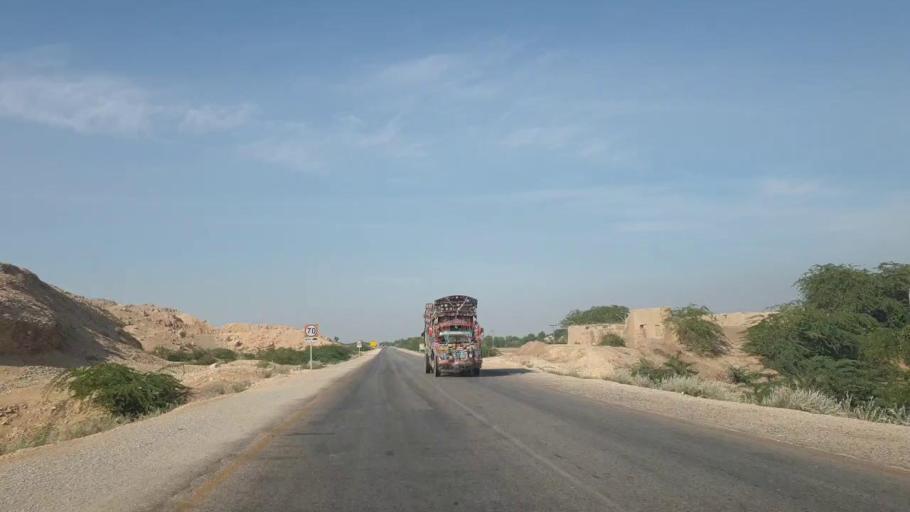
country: PK
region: Sindh
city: Sehwan
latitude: 26.3060
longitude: 67.8931
